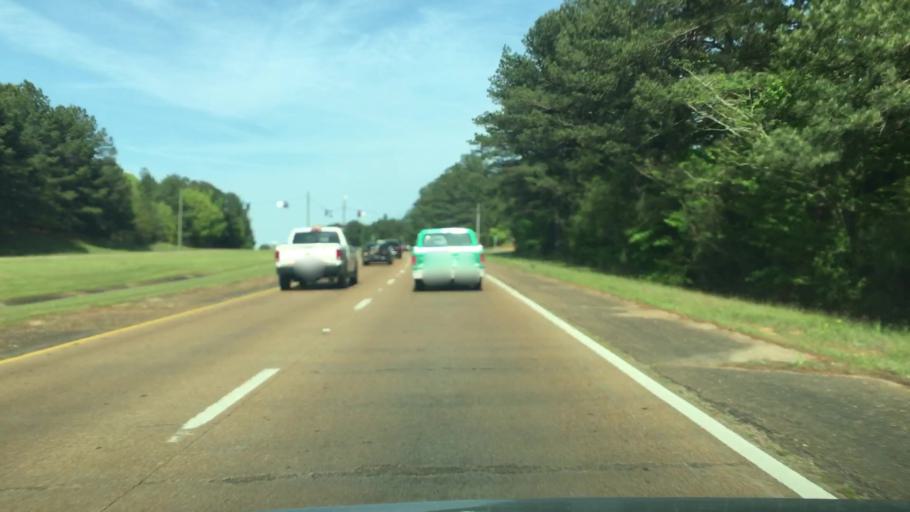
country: US
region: Mississippi
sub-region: Rankin County
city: Brandon
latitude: 32.3614
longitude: -89.9959
